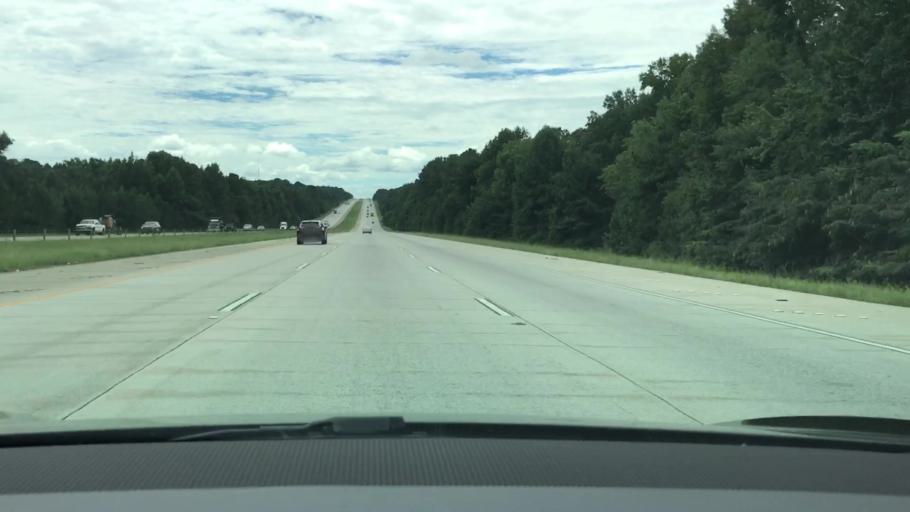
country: US
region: Georgia
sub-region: Coweta County
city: East Newnan
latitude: 33.2982
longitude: -84.7934
